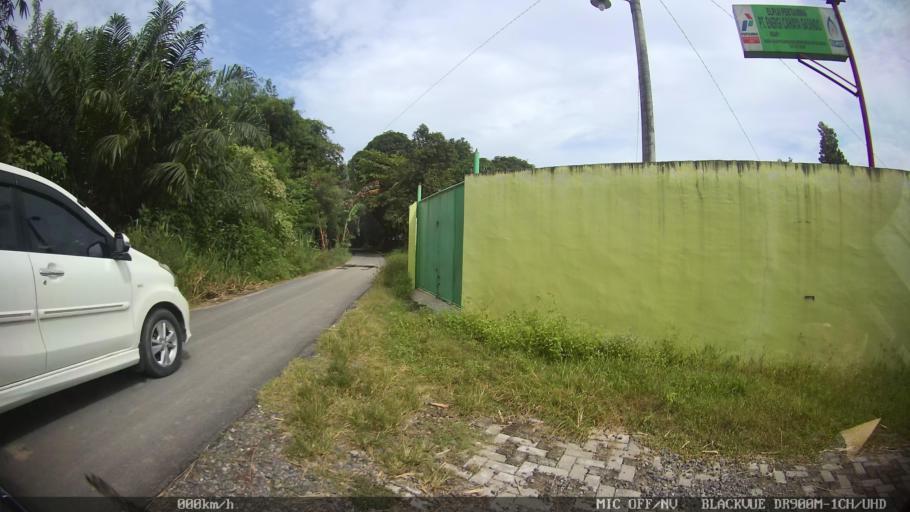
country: ID
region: North Sumatra
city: Percut
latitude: 3.6208
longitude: 98.7907
